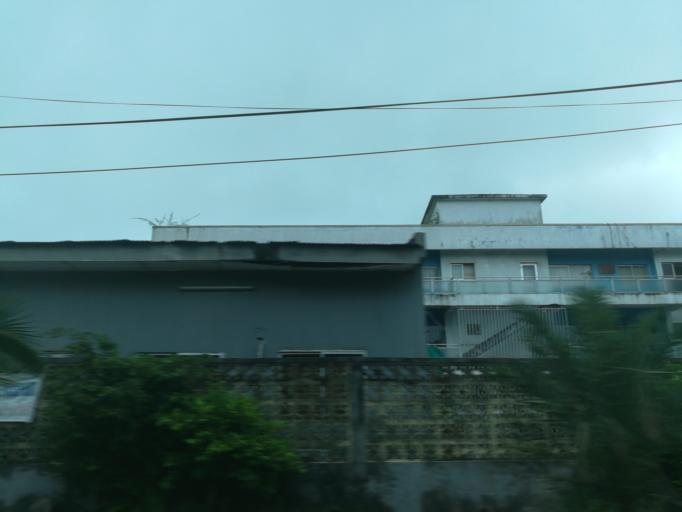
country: NG
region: Lagos
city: Ikoyi
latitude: 6.4239
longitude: 3.4222
